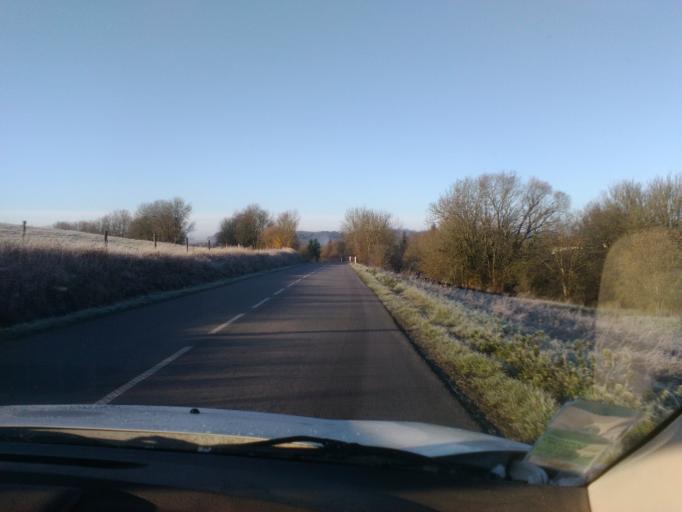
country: FR
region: Lorraine
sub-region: Departement des Vosges
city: Darnieulles
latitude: 48.1843
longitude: 6.2160
